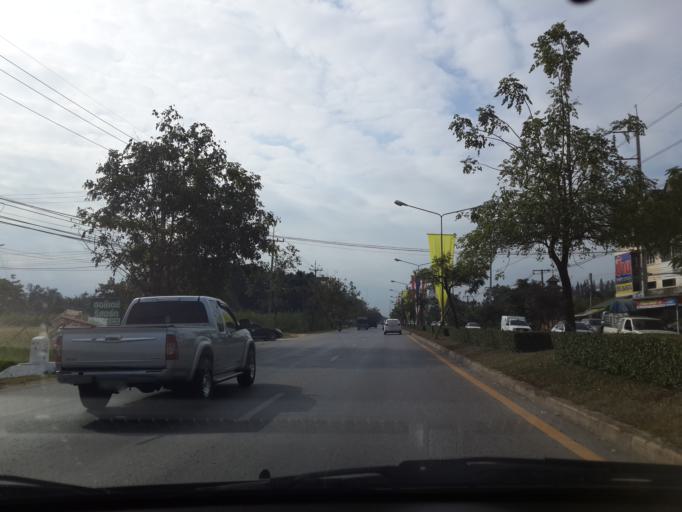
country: TH
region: Chiang Mai
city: San Sai
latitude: 18.8550
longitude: 99.0143
